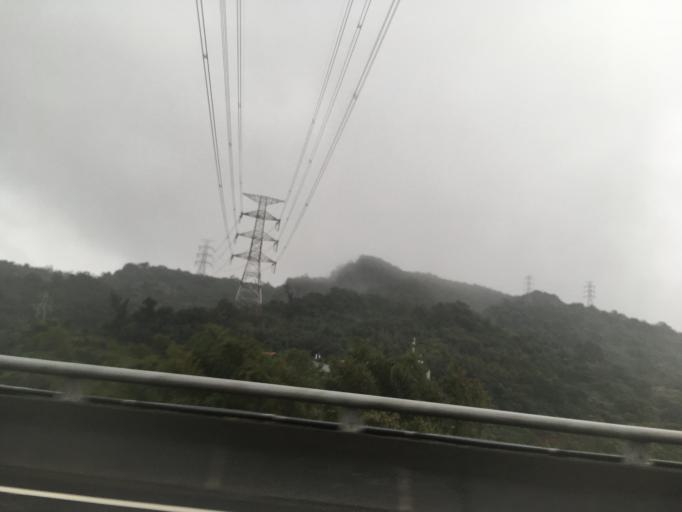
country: TW
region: Taiwan
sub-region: Keelung
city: Keelung
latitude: 25.0858
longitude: 121.6771
